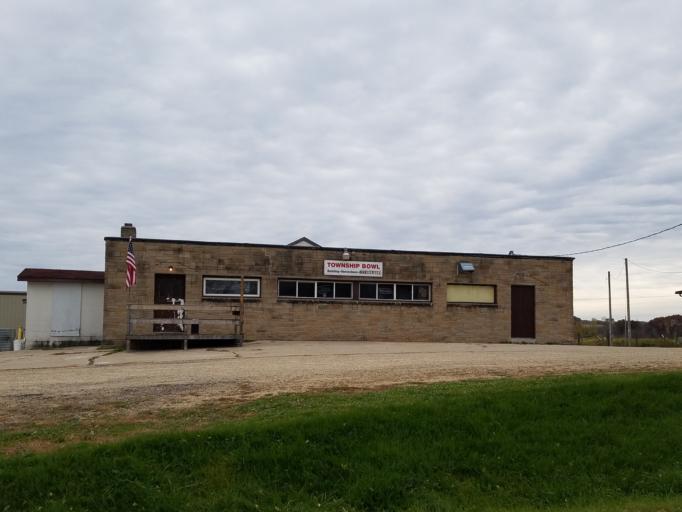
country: US
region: Wisconsin
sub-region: Vernon County
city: Hillsboro
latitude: 43.6593
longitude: -90.3315
